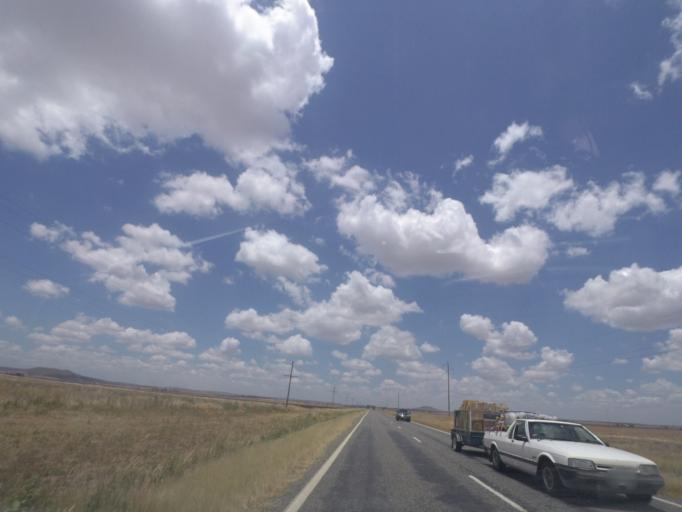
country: AU
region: Queensland
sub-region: Toowoomba
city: Top Camp
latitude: -27.9034
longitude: 151.9771
